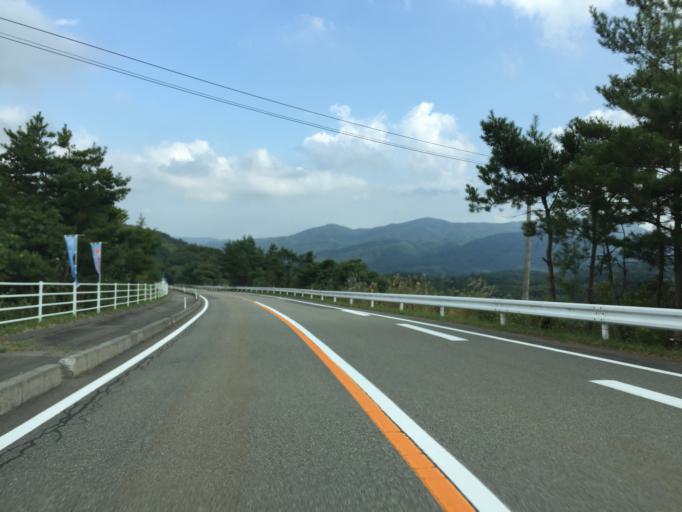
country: JP
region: Fukushima
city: Funehikimachi-funehiki
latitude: 37.5740
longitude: 140.7304
